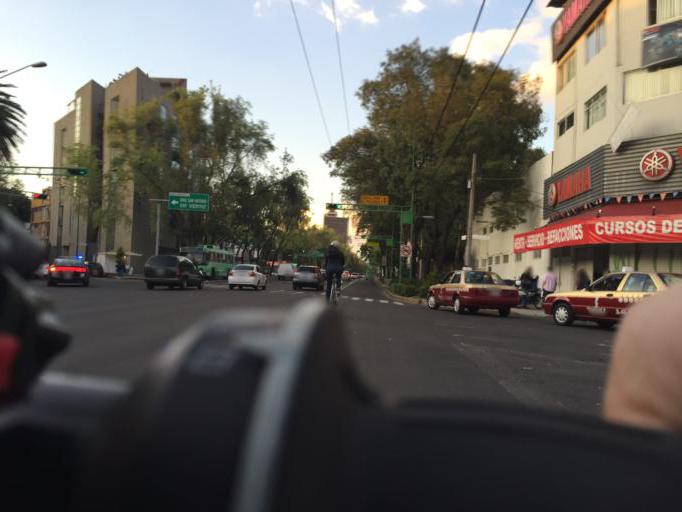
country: MX
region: Mexico City
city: Colonia Nativitas
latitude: 19.3866
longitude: -99.1471
